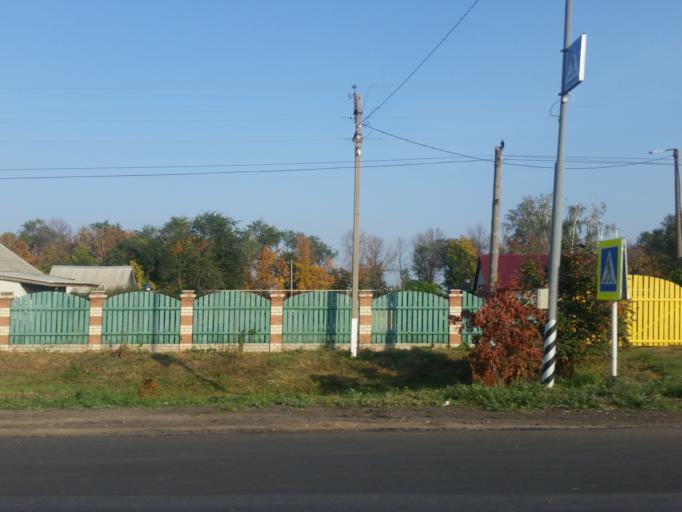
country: RU
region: Ulyanovsk
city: Mirnyy
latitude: 54.3696
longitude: 48.7226
